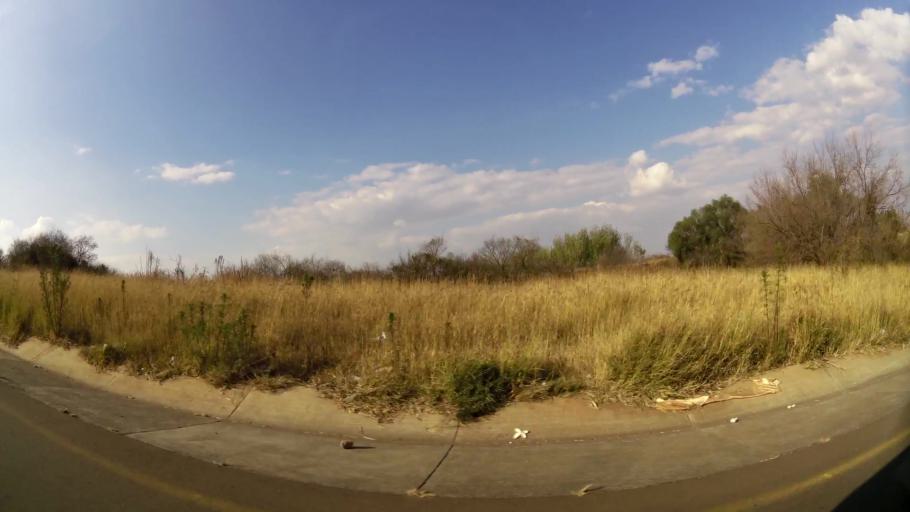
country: ZA
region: Gauteng
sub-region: Ekurhuleni Metropolitan Municipality
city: Tembisa
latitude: -25.9214
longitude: 28.2272
